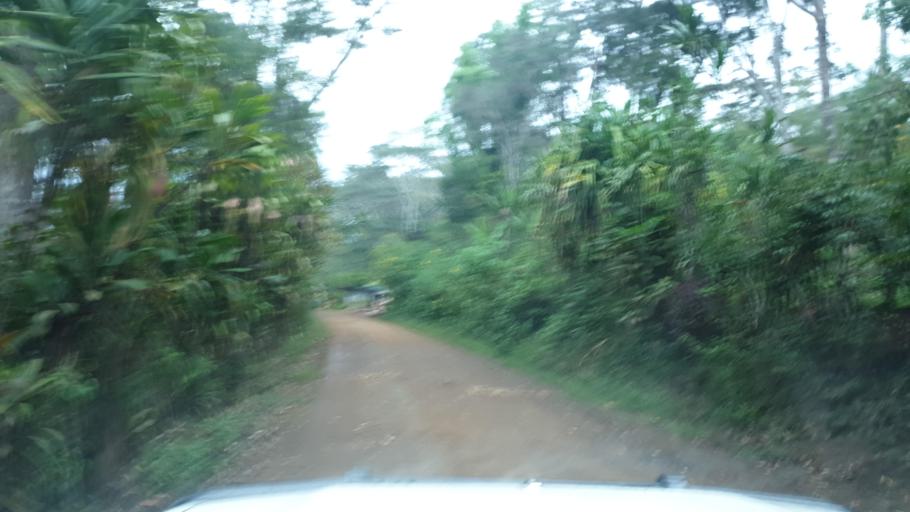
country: PG
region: Eastern Highlands
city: Goroka
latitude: -5.9712
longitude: 145.2762
